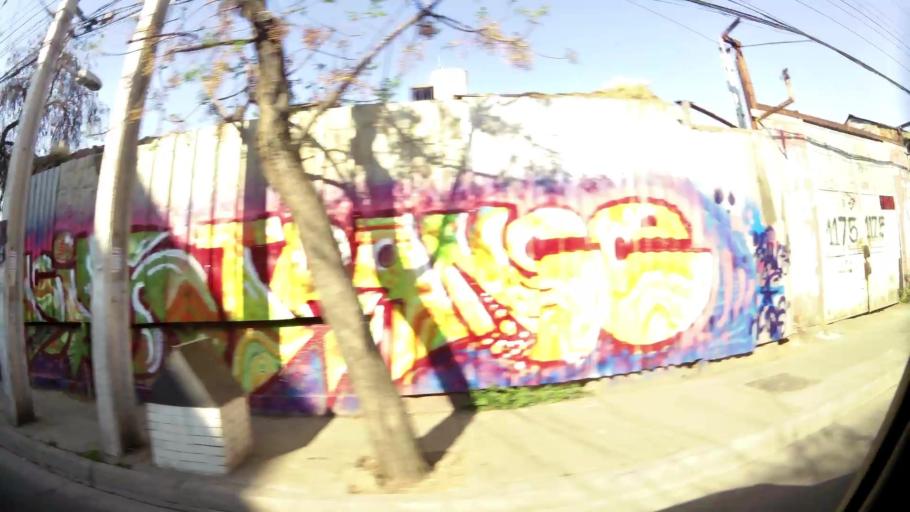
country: CL
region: Santiago Metropolitan
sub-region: Provincia de Santiago
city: Santiago
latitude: -33.4319
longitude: -70.6764
